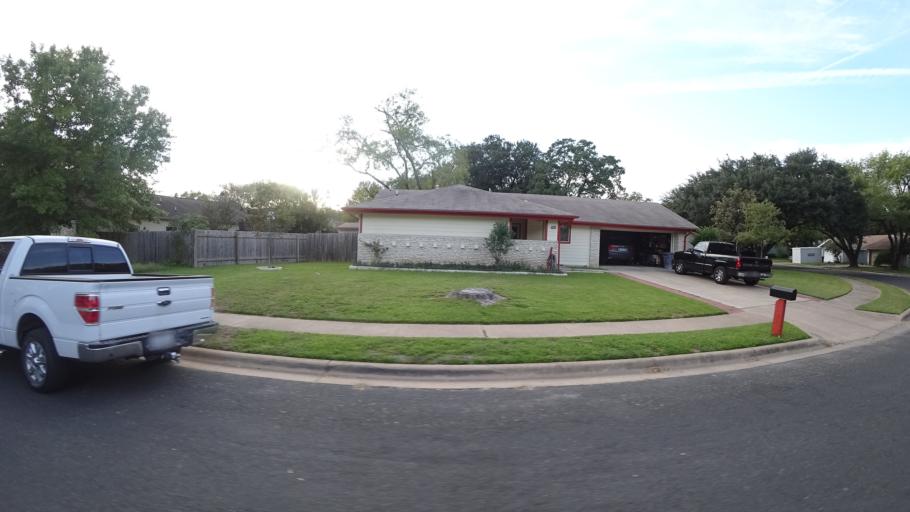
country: US
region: Texas
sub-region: Travis County
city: Austin
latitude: 30.2052
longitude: -97.7674
